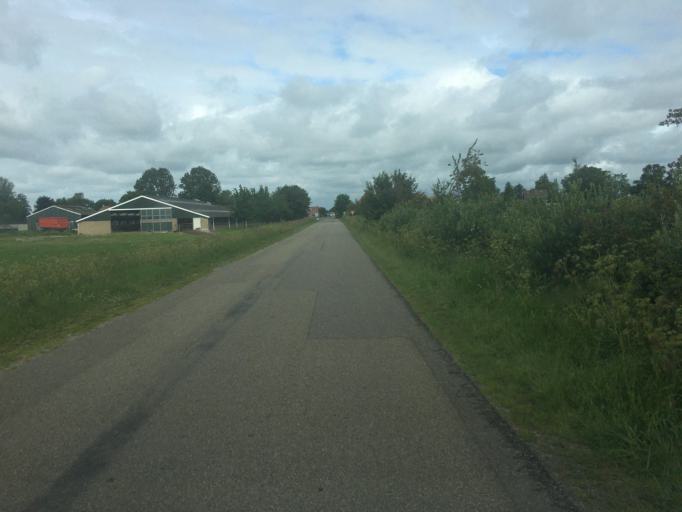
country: NL
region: Friesland
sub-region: Gemeente Skarsterlan
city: Oudehaske
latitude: 52.9174
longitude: 5.8551
